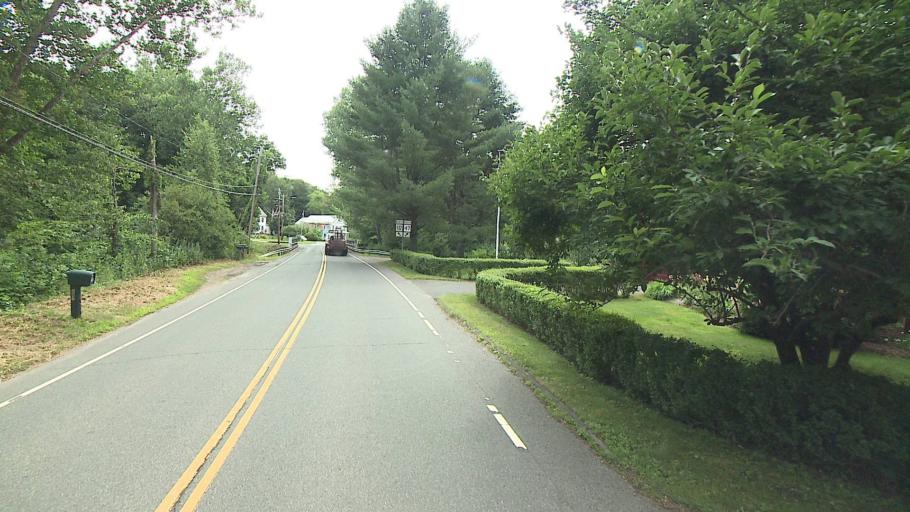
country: US
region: Connecticut
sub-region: Litchfield County
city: Woodbury
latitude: 41.5673
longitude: -73.2188
